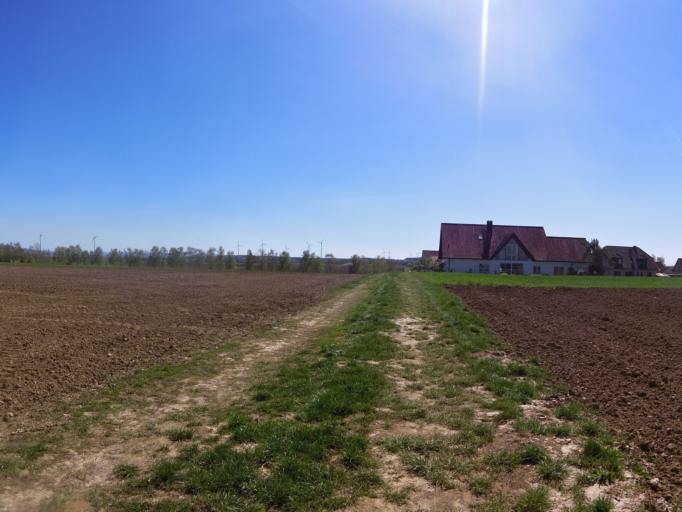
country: DE
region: Bavaria
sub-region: Regierungsbezirk Unterfranken
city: Biebelried
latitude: 49.7992
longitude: 10.0894
